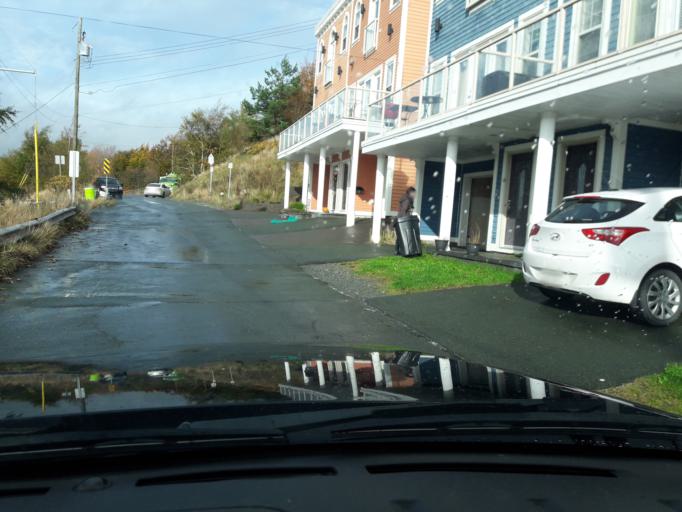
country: CA
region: Newfoundland and Labrador
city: St. John's
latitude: 47.5704
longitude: -52.6935
